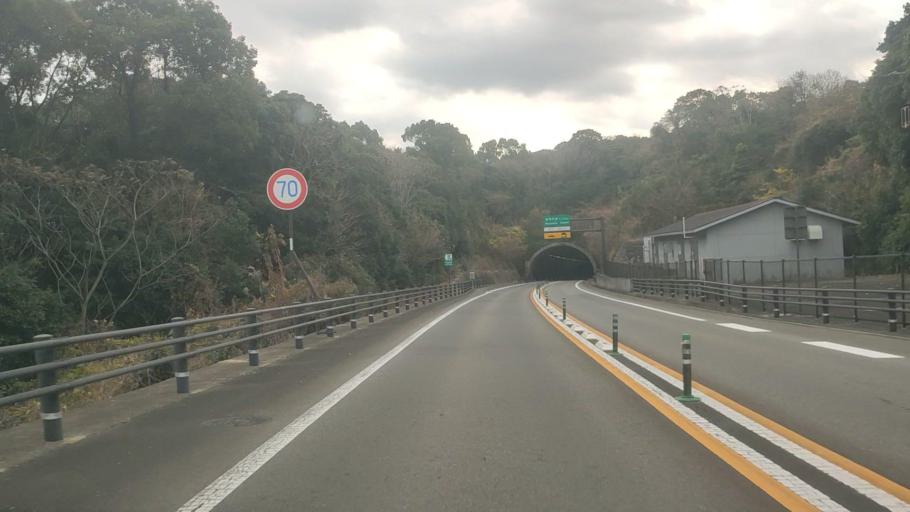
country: JP
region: Nagasaki
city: Shimabara
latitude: 32.7800
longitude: 130.3555
